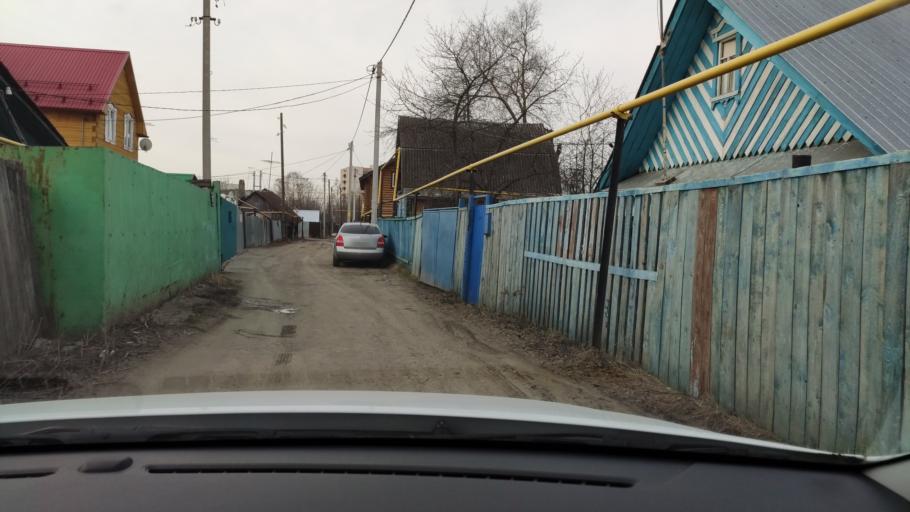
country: RU
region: Tatarstan
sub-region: Gorod Kazan'
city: Kazan
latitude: 55.7447
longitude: 49.1486
